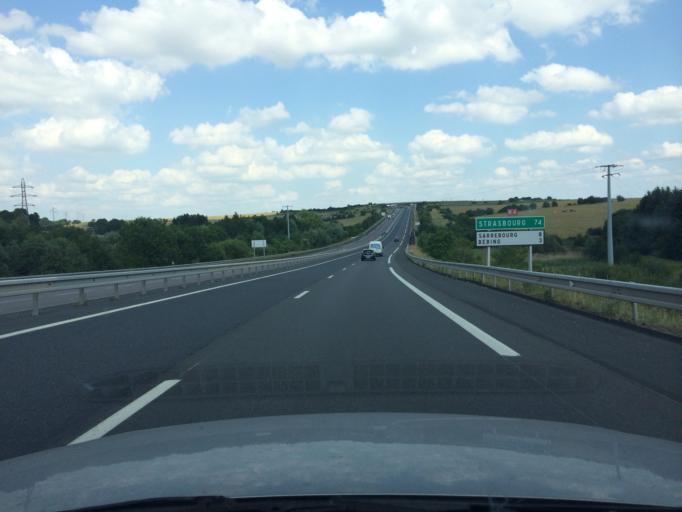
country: FR
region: Lorraine
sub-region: Departement de la Moselle
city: Lorquin
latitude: 48.6994
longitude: 6.9662
